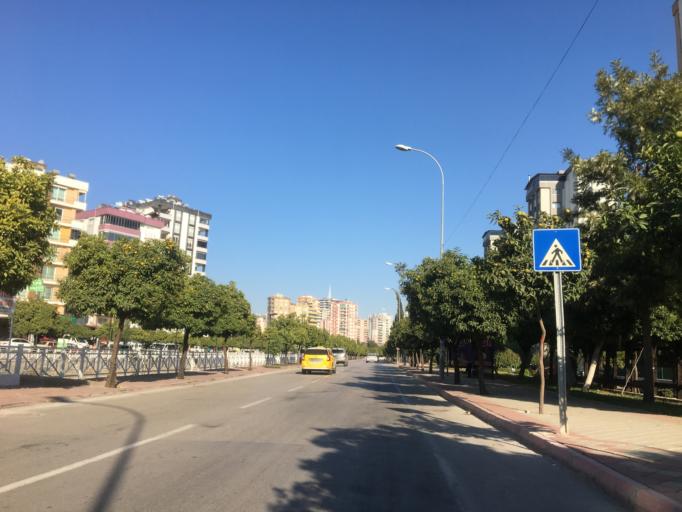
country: TR
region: Adana
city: Seyhan
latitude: 37.0283
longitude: 35.2779
